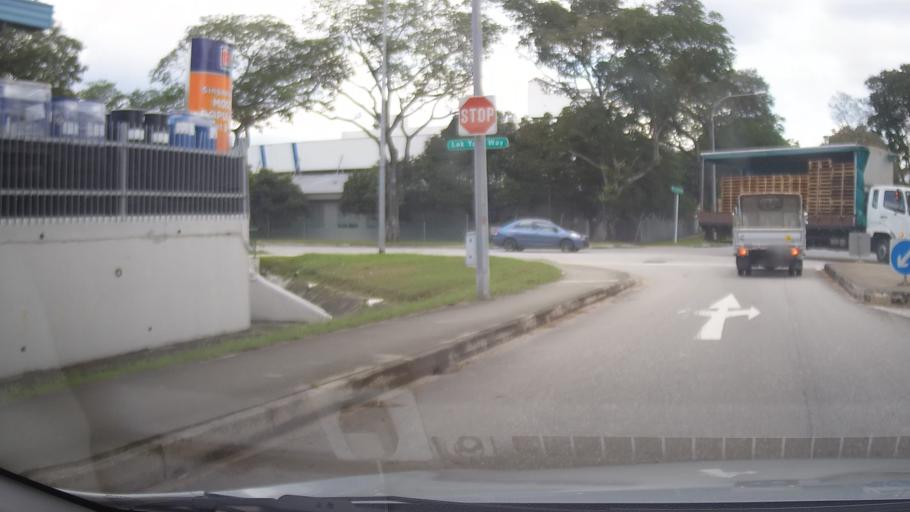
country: MY
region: Johor
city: Johor Bahru
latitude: 1.3243
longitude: 103.6935
